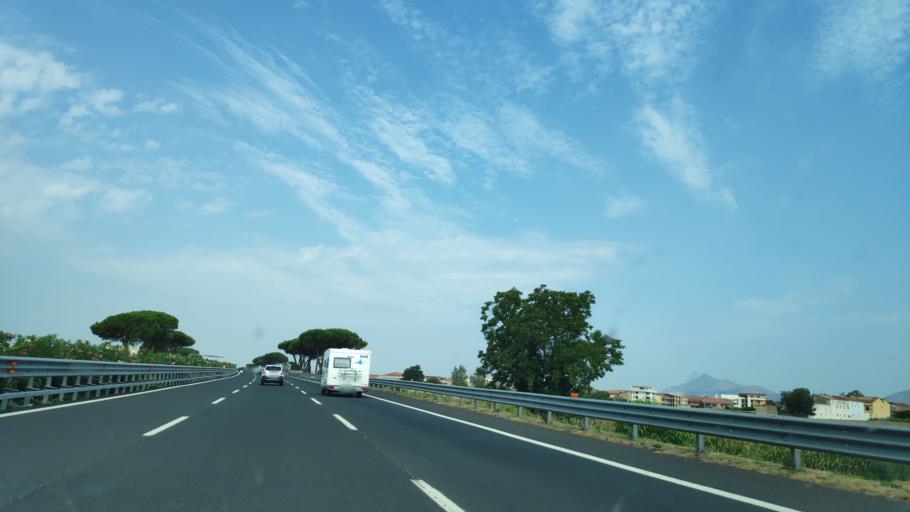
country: IT
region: Campania
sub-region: Provincia di Caserta
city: San Marco Evangelista
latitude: 41.0304
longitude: 14.3471
